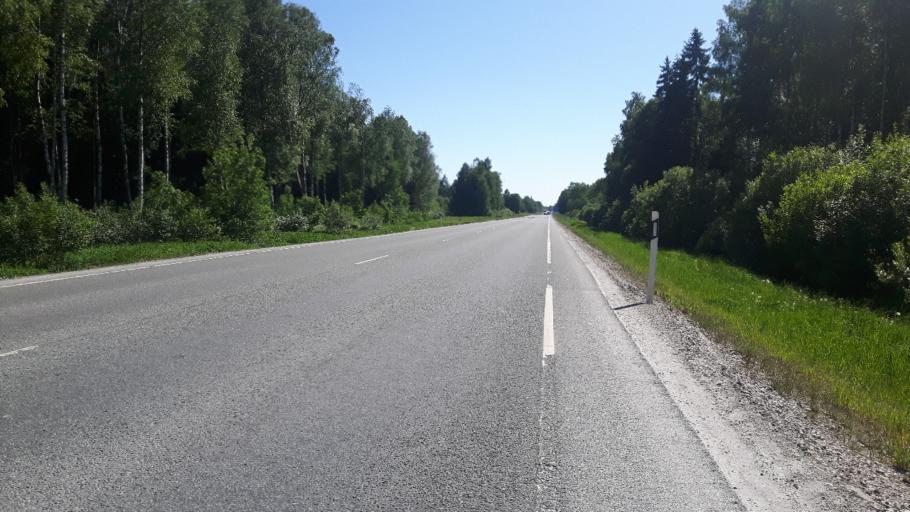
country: EE
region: Raplamaa
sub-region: Rapla vald
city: Rapla
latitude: 59.0220
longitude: 24.8102
